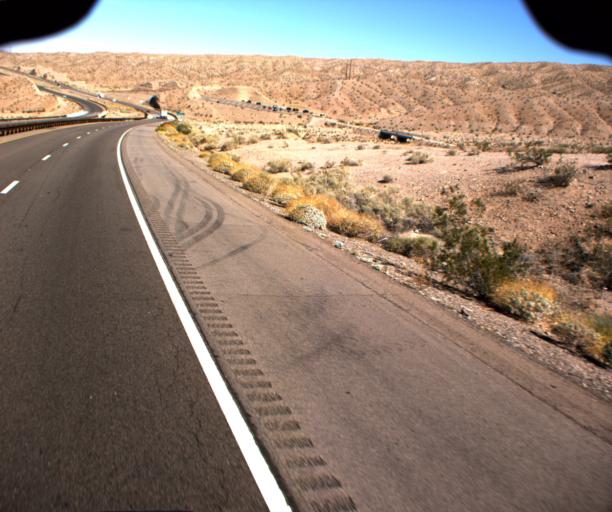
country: US
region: Nevada
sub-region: Clark County
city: Boulder City
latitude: 35.9767
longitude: -114.6955
